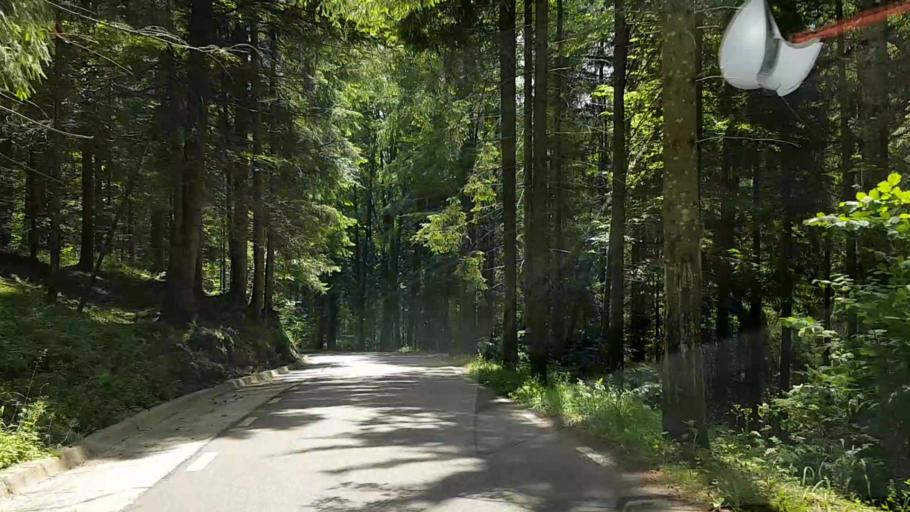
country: RO
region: Suceava
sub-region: Comuna Crucea
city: Crucea
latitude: 47.4238
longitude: 25.5756
